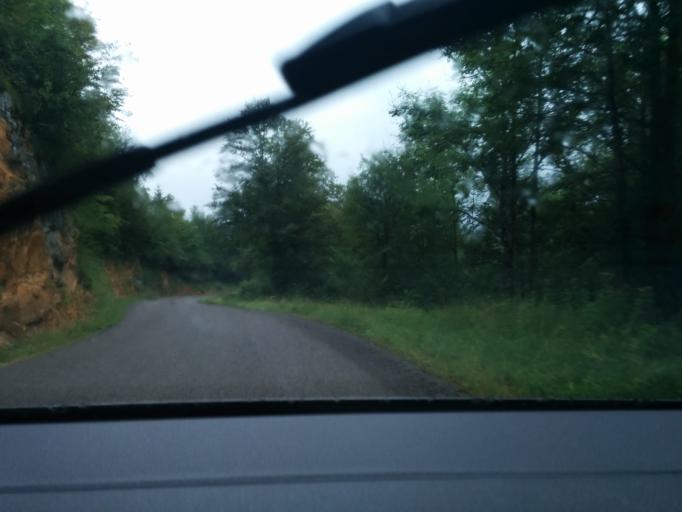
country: FR
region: Franche-Comte
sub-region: Departement du Jura
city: Valfin-les-Saint-Claude
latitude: 46.4384
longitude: 5.8160
